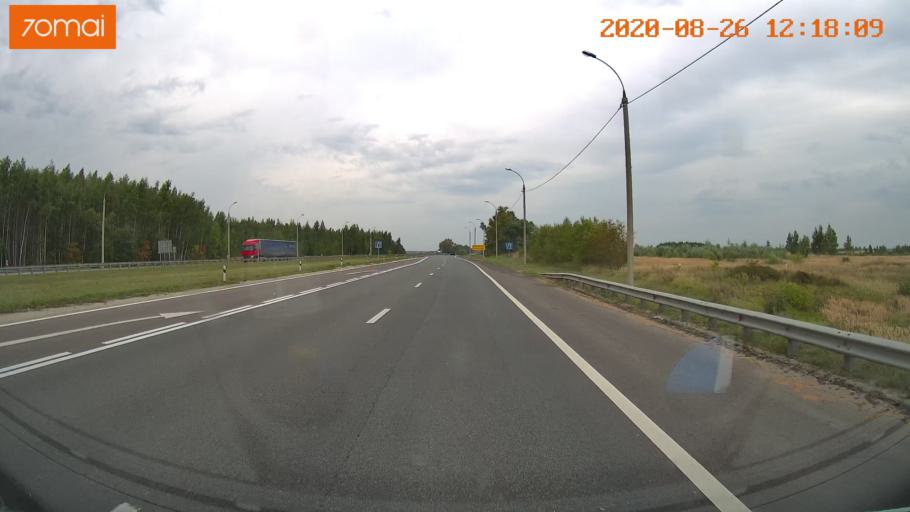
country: RU
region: Rjazan
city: Murmino
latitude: 54.4703
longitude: 40.0229
